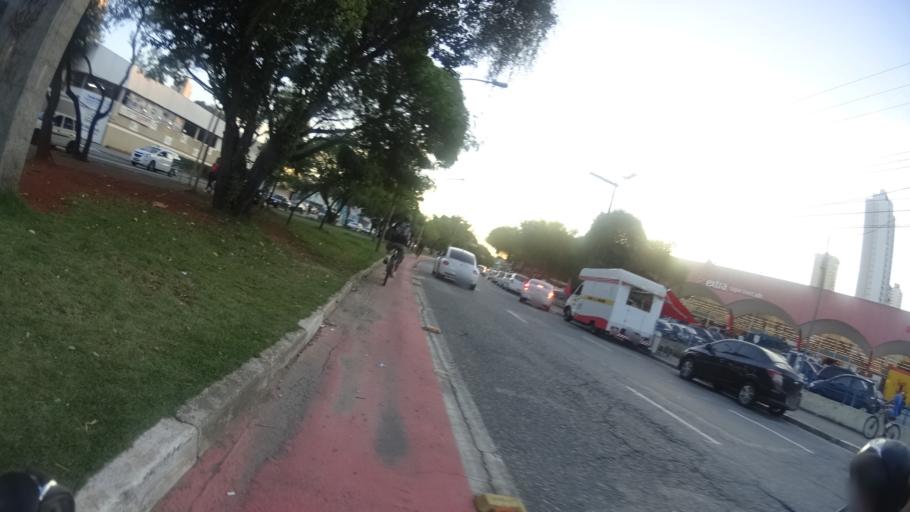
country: BR
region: Sao Paulo
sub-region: Sao Paulo
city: Sao Paulo
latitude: -23.4865
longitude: -46.6403
